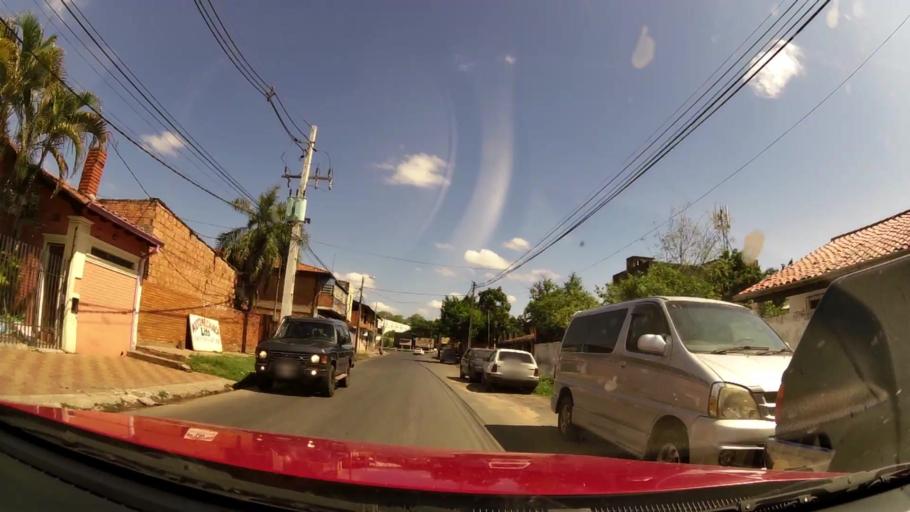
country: PY
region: Central
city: Fernando de la Mora
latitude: -25.2555
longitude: -57.5535
